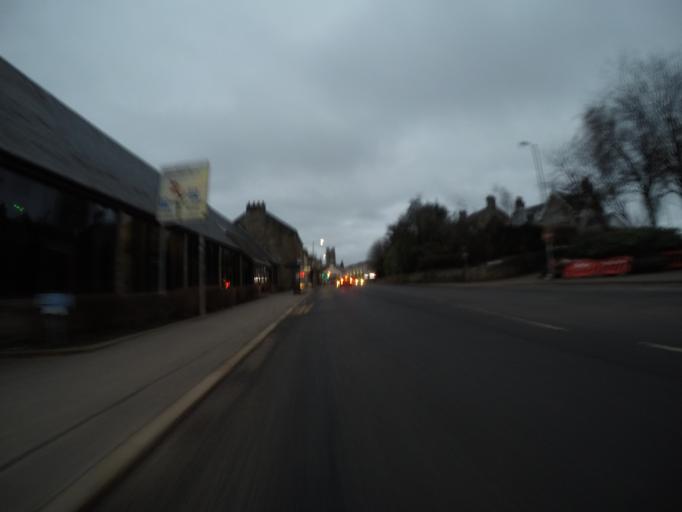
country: GB
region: Scotland
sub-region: North Ayrshire
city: Kilwinning
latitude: 55.6539
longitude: -4.7038
